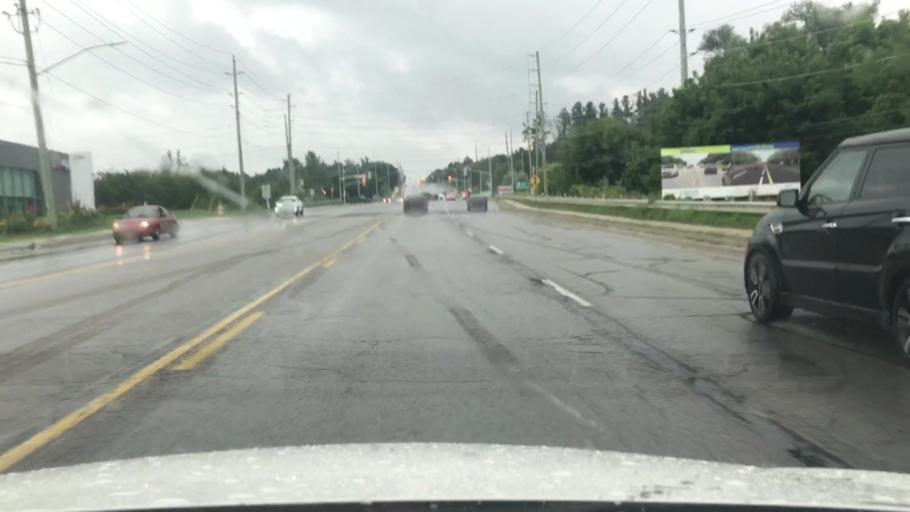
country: CA
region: Ontario
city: Newmarket
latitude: 44.0514
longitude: -79.4283
